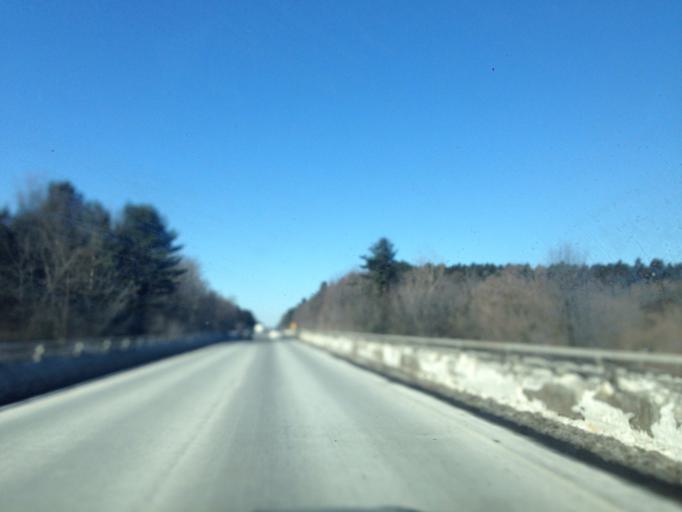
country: CA
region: Ontario
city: Ottawa
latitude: 45.3629
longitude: -75.4855
